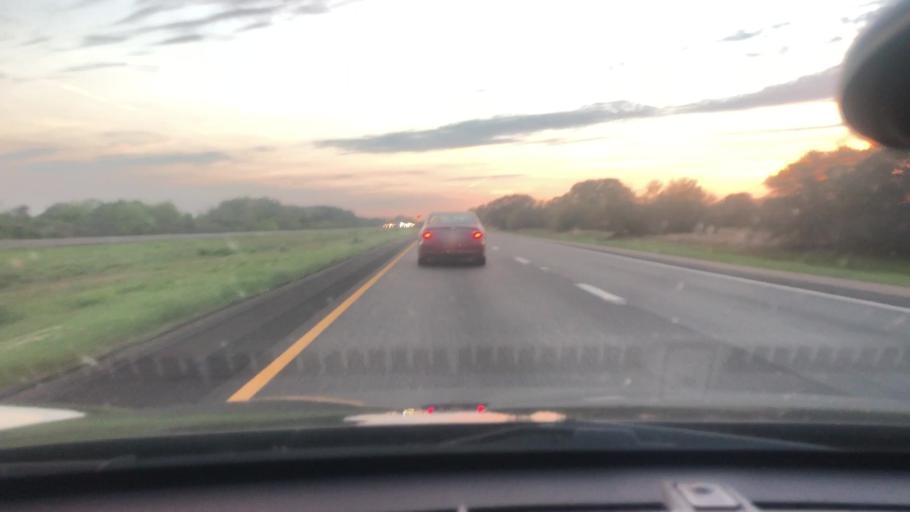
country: US
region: Texas
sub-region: Victoria County
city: Inez
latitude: 28.9197
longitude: -96.7614
